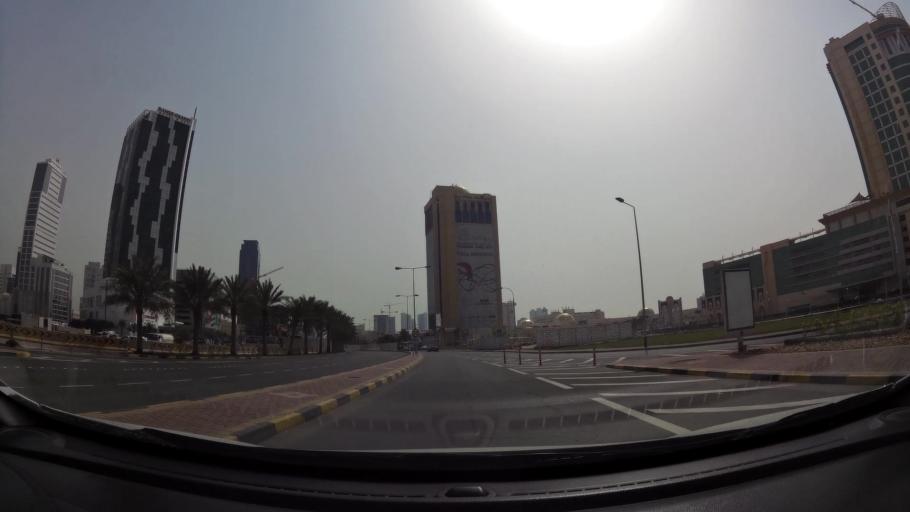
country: BH
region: Manama
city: Jidd Hafs
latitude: 26.2347
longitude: 50.5343
